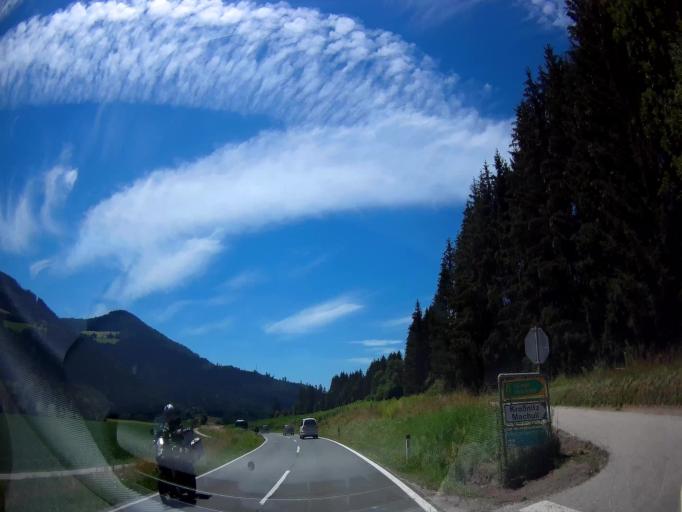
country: AT
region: Carinthia
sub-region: Politischer Bezirk Sankt Veit an der Glan
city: Strassburg
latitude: 46.8968
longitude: 14.3509
